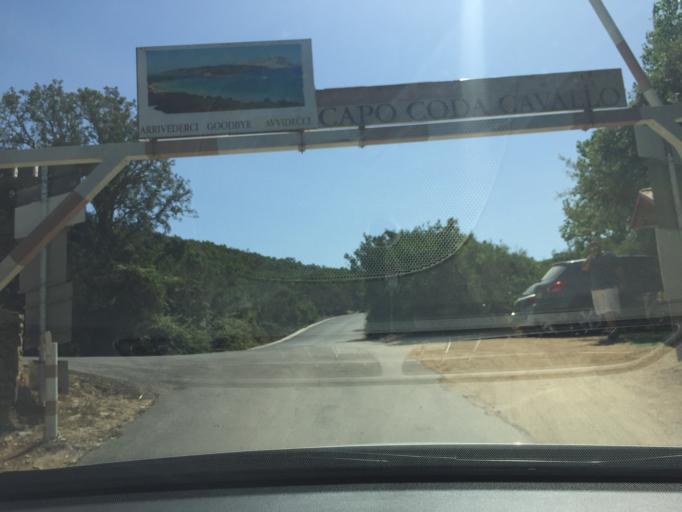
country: IT
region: Sardinia
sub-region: Provincia di Olbia-Tempio
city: San Teodoro
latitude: 40.8400
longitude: 9.7116
